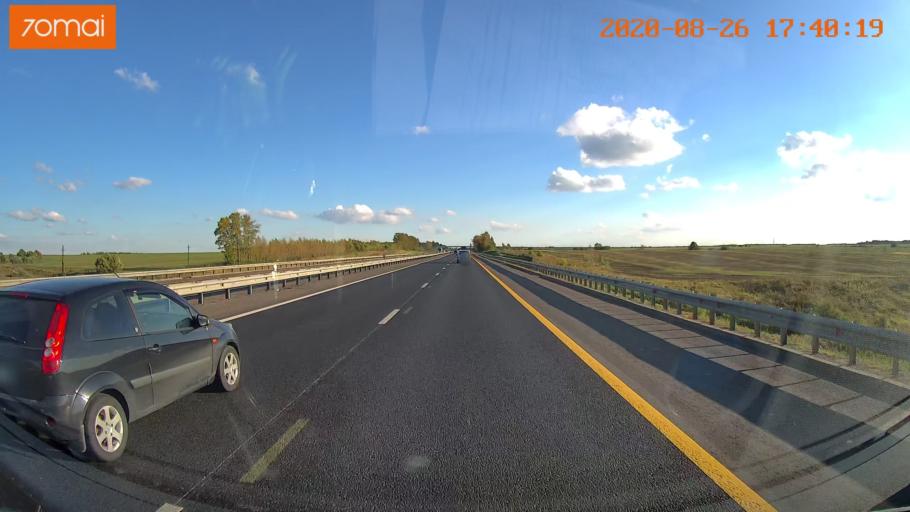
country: RU
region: Tula
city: Kazachka
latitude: 53.3139
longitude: 38.1787
